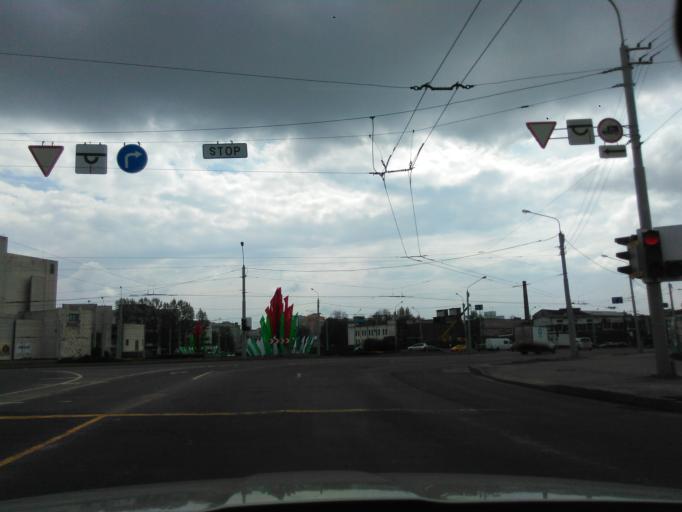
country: BY
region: Minsk
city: Minsk
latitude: 53.8973
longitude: 27.5372
